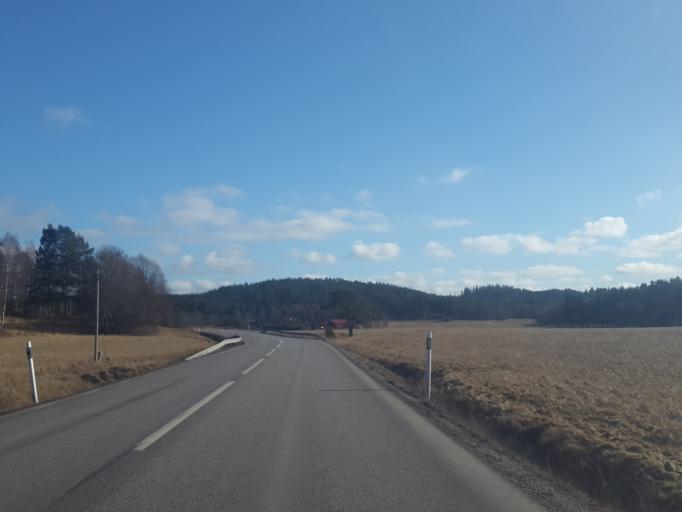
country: SE
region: Vaestra Goetaland
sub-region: Alingsas Kommun
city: Alingsas
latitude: 57.9542
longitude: 12.4608
